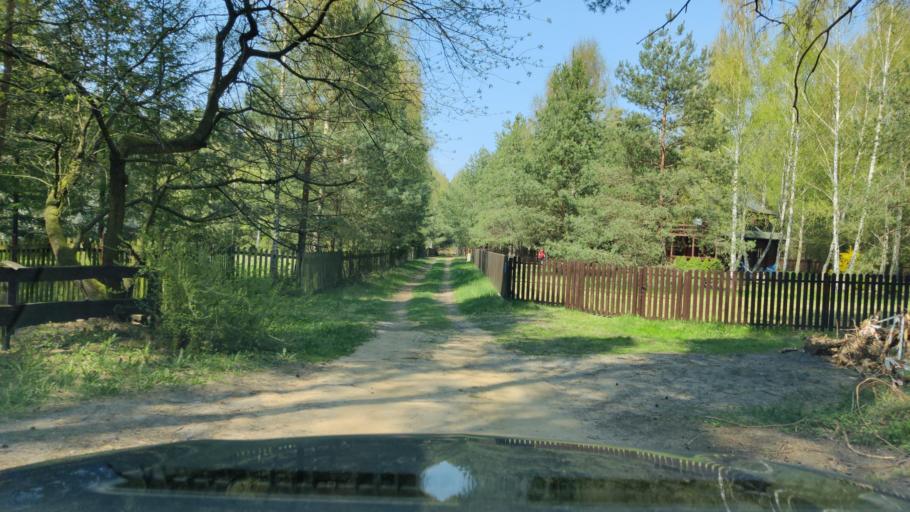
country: PL
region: Masovian Voivodeship
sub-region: Powiat pultuski
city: Obryte
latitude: 52.7527
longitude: 21.2012
